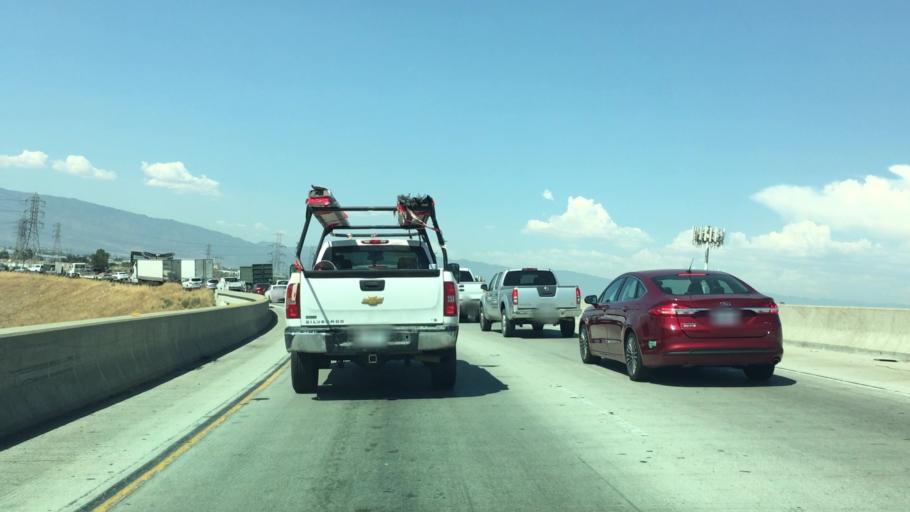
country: US
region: California
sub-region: Riverside County
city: Mira Loma
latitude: 34.0230
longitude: -117.5497
